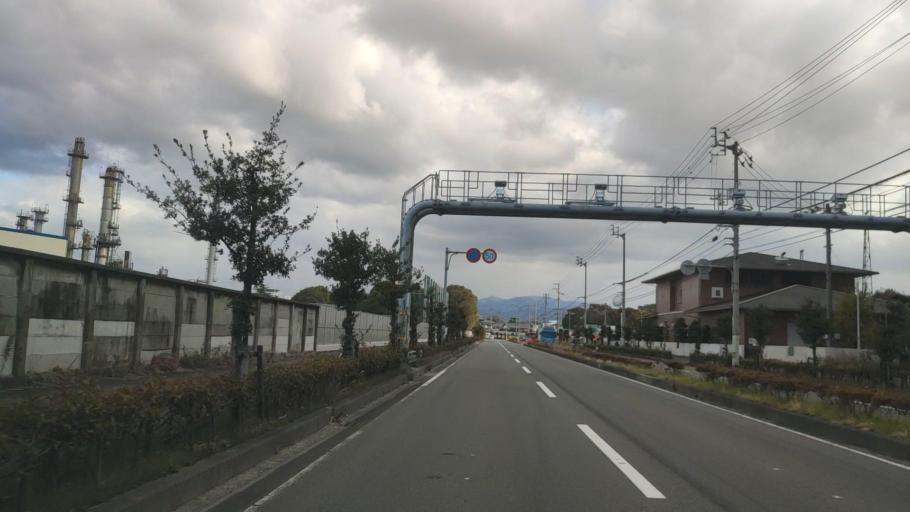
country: JP
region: Ehime
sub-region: Shikoku-chuo Shi
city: Matsuyama
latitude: 33.8460
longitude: 132.7102
